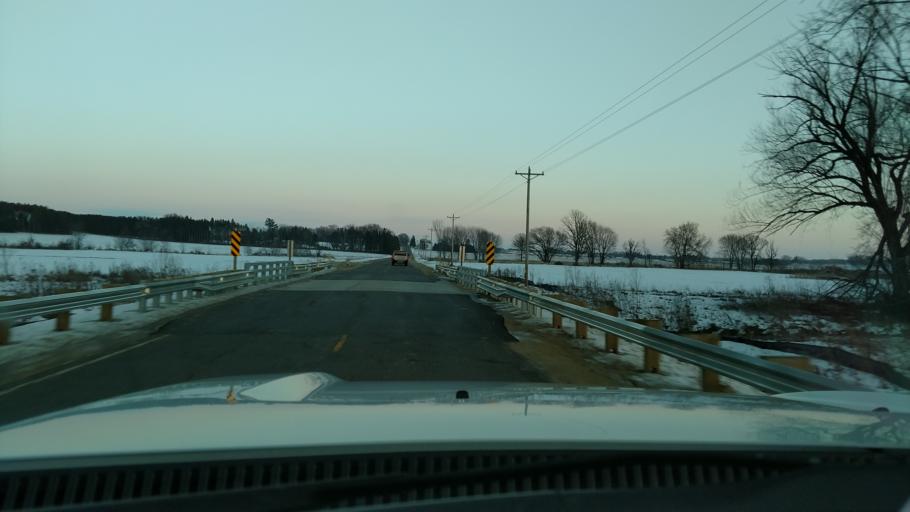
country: US
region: Wisconsin
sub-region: Saint Croix County
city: Roberts
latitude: 44.9132
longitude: -92.4998
